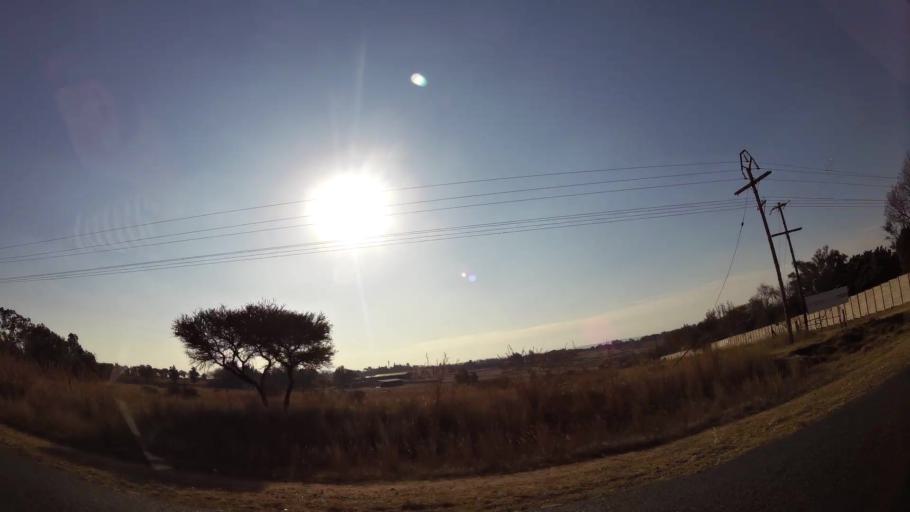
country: ZA
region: Gauteng
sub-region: West Rand District Municipality
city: Muldersdriseloop
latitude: -26.0154
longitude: 27.8869
